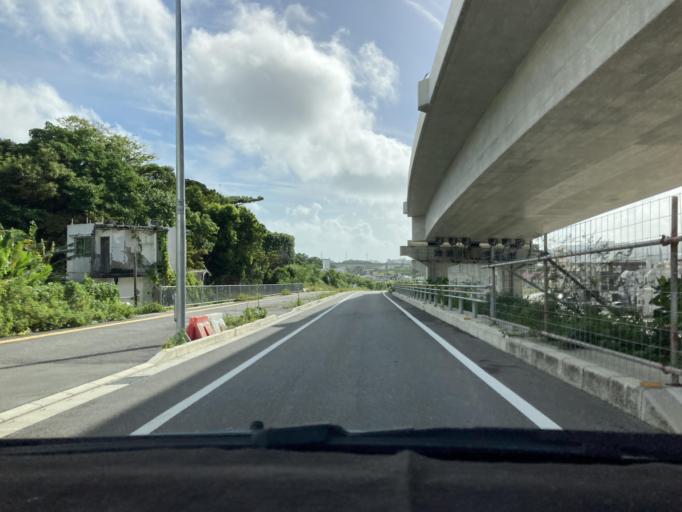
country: JP
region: Okinawa
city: Naha-shi
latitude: 26.2062
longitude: 127.7309
